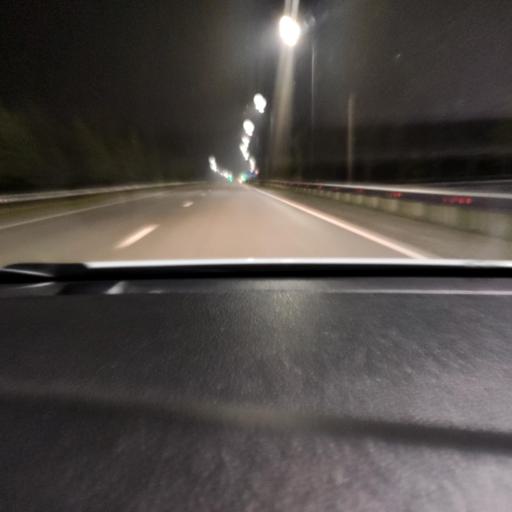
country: RU
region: Tatarstan
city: Stolbishchi
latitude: 55.6371
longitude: 49.1093
